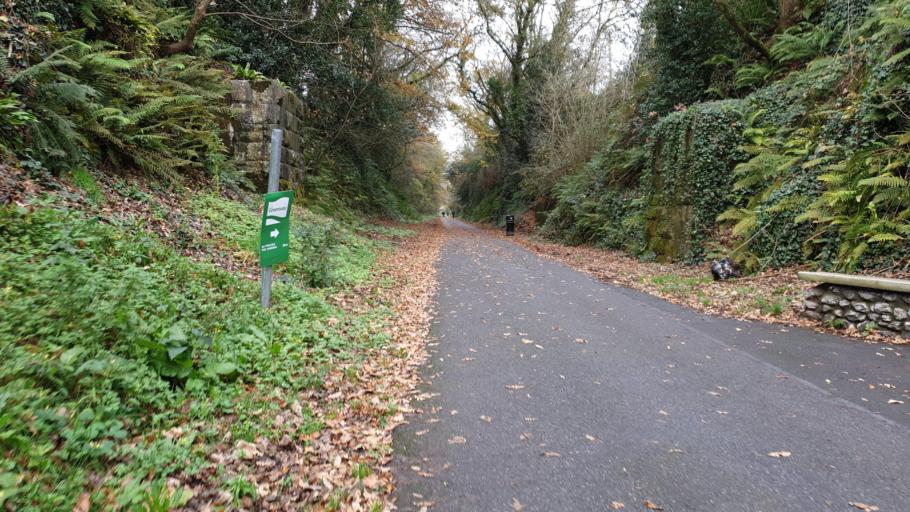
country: IE
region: Munster
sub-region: County Cork
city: Cork
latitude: 51.8875
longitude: -8.4087
